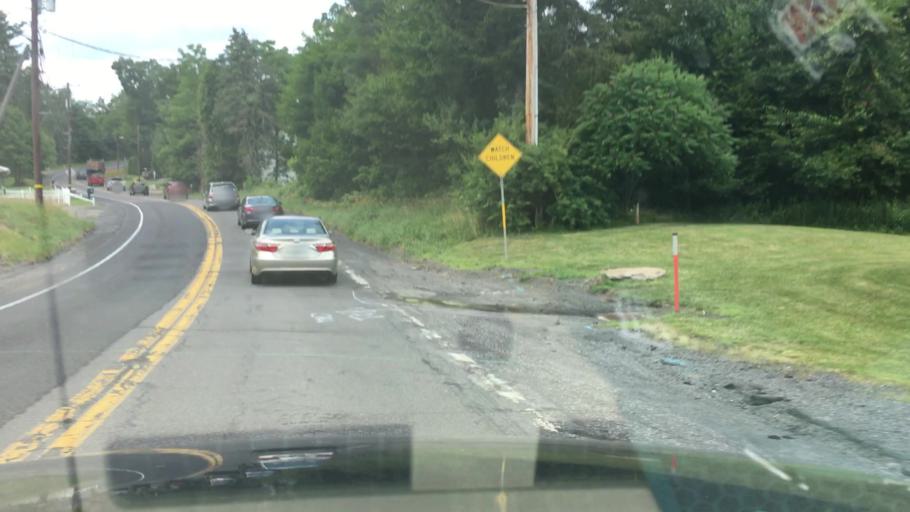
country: US
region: Pennsylvania
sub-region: Schuylkill County
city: Minersville
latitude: 40.7035
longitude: -76.3263
